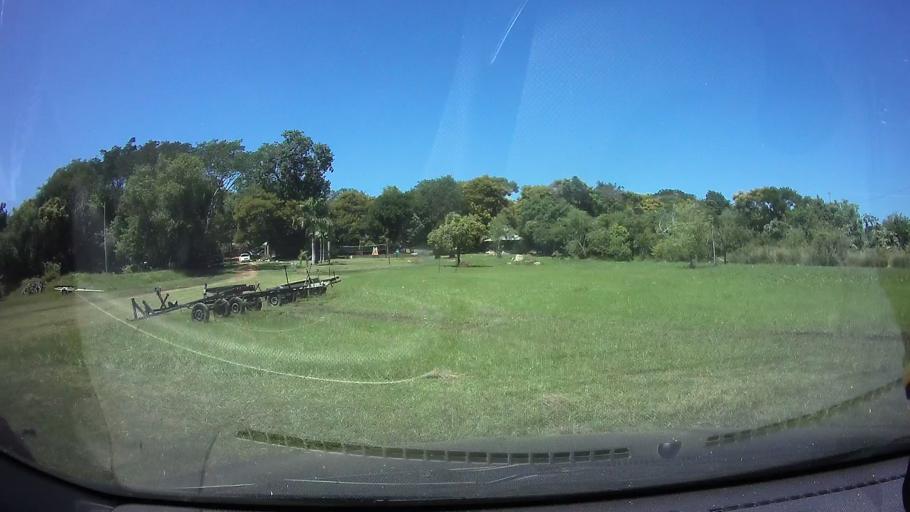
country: PY
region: Cordillera
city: Arroyos y Esteros
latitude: -24.9746
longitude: -57.2139
